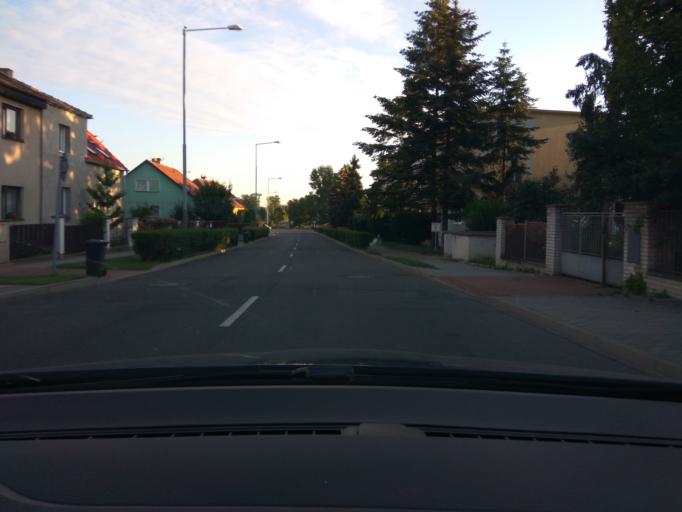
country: CZ
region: Praha
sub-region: Praha 18
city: Letnany
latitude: 50.1543
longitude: 14.5285
